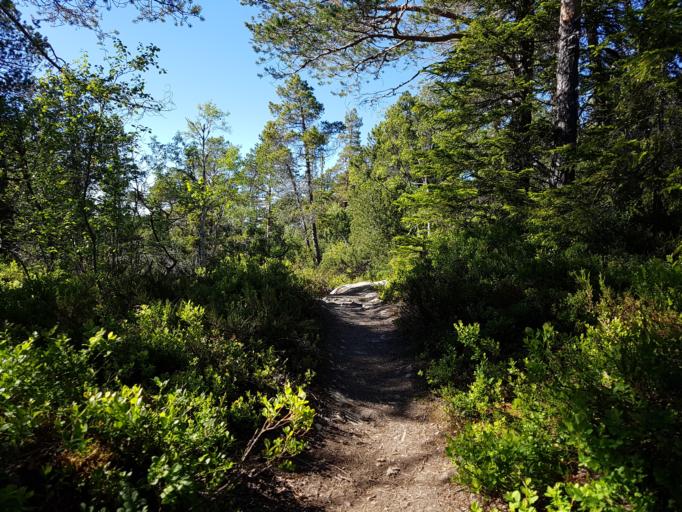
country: NO
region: Sor-Trondelag
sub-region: Trondheim
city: Trondheim
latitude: 63.4117
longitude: 10.3095
